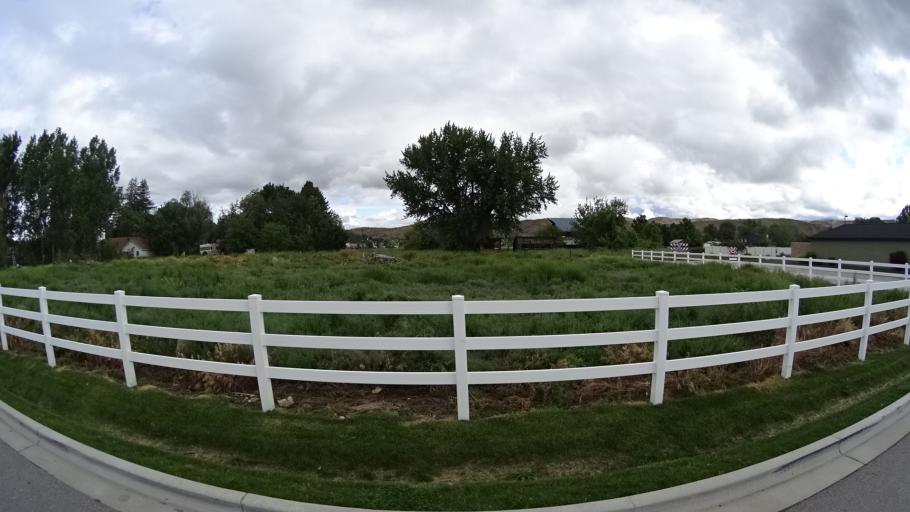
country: US
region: Idaho
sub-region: Ada County
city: Eagle
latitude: 43.6770
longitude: -116.2928
